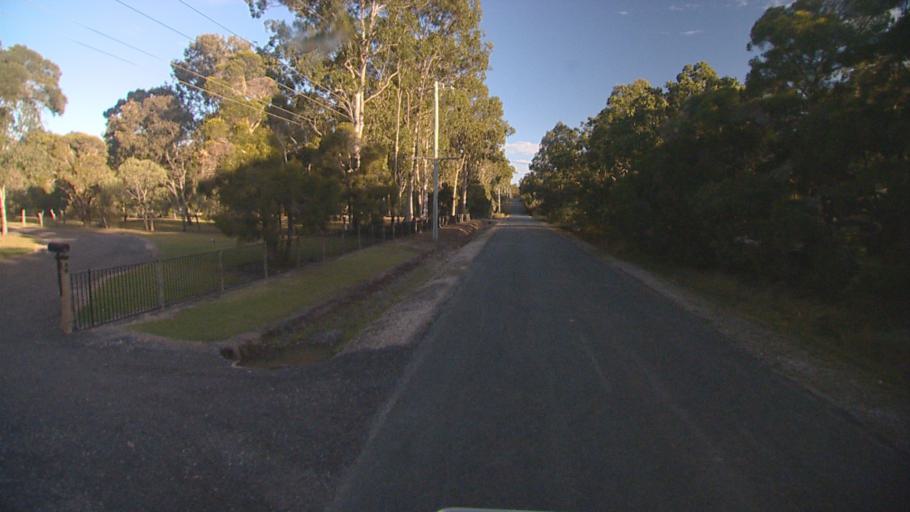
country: AU
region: Queensland
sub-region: Logan
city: Waterford West
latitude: -27.7224
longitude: 153.1419
